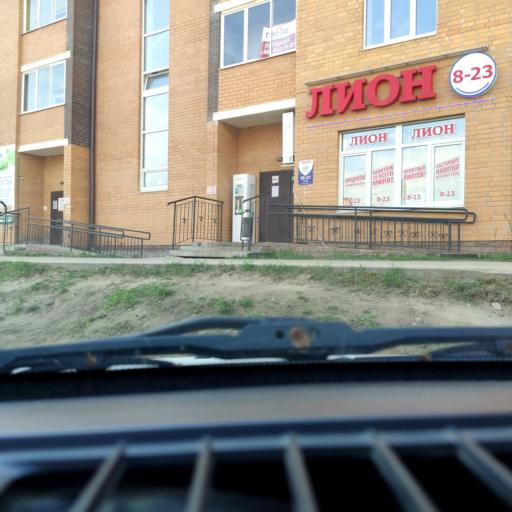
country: RU
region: Perm
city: Ust'-Kachka
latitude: 58.0032
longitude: 55.6766
